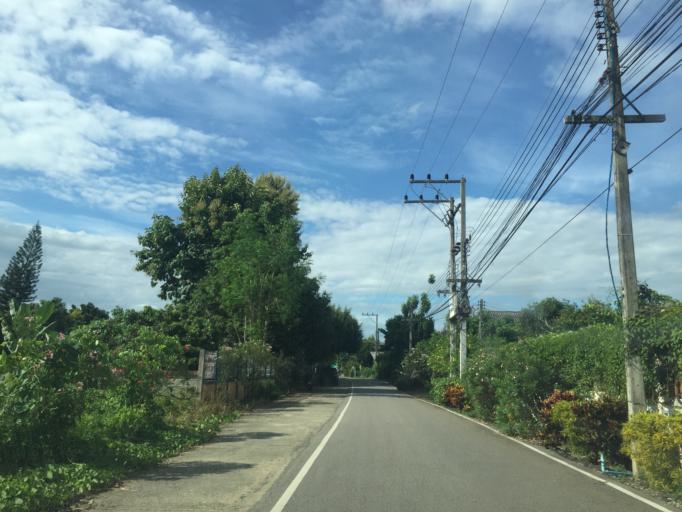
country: TH
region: Lamphun
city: Lamphun
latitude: 18.6338
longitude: 99.0448
